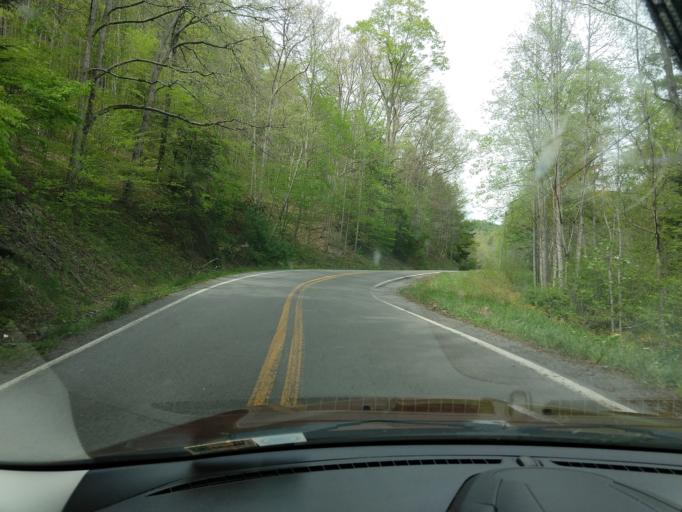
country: US
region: West Virginia
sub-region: McDowell County
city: Welch
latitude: 37.3528
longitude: -81.6642
